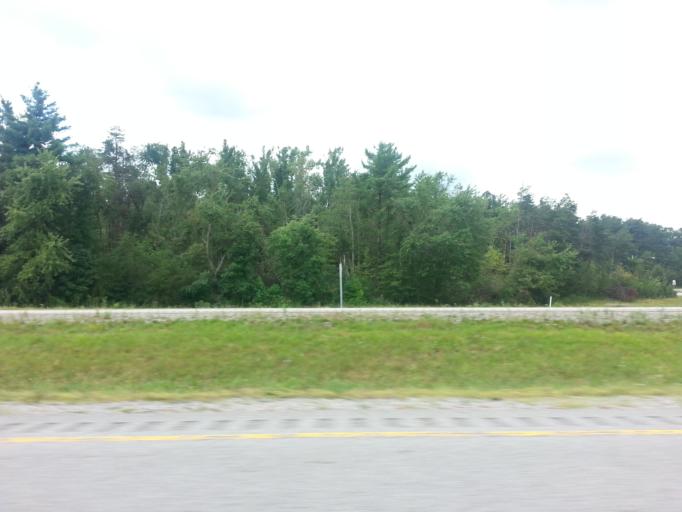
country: US
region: Tennessee
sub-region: Putnam County
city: Monterey
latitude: 36.1377
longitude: -85.2652
